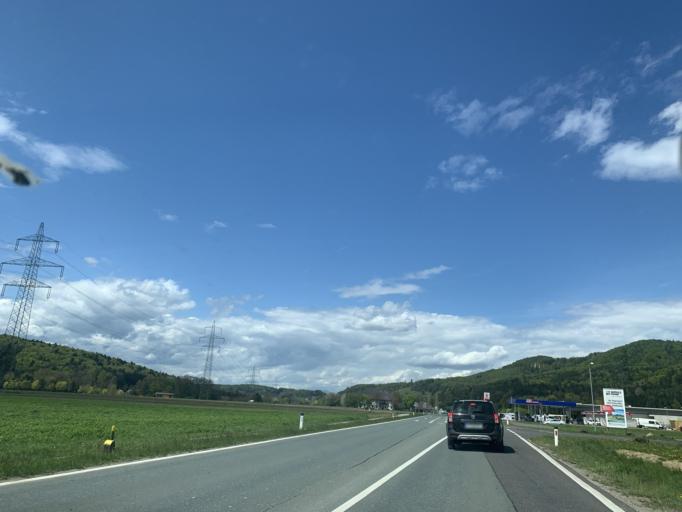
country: AT
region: Styria
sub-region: Politischer Bezirk Leibnitz
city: Lang
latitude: 46.8498
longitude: 15.5149
